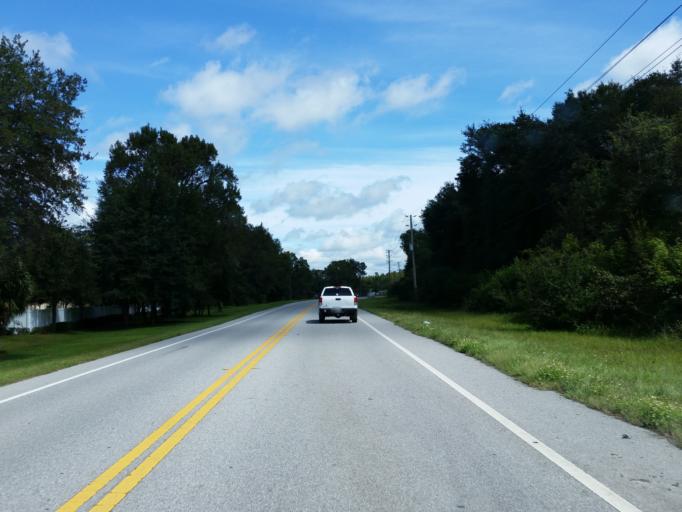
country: US
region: Florida
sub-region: Pasco County
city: Wesley Chapel
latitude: 28.2192
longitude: -82.3868
